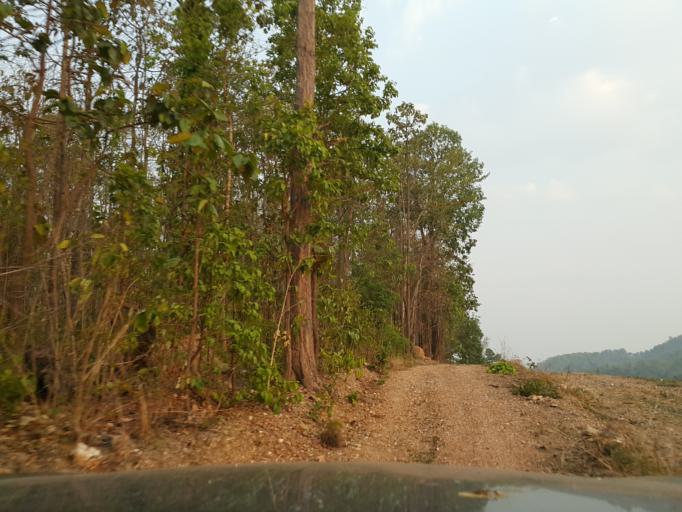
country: TH
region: Lamphun
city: Thung Hua Chang
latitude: 17.9164
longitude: 99.0729
